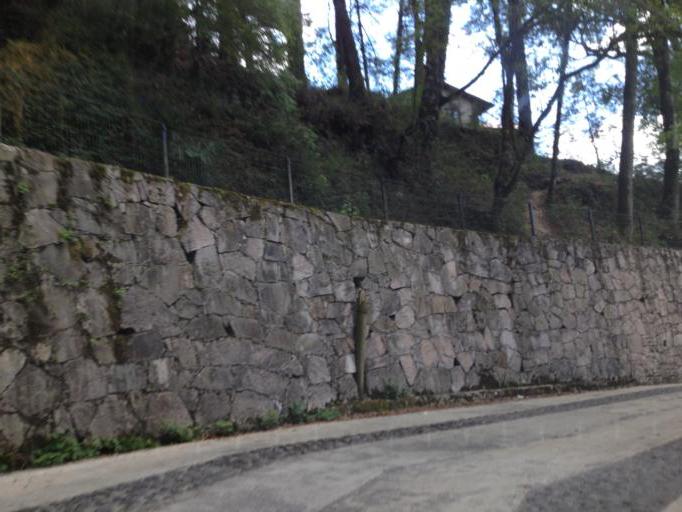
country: MX
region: Hidalgo
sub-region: Pachuca de Soto
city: San Miguel Cerezo (El Cerezo)
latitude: 20.2153
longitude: -98.7254
